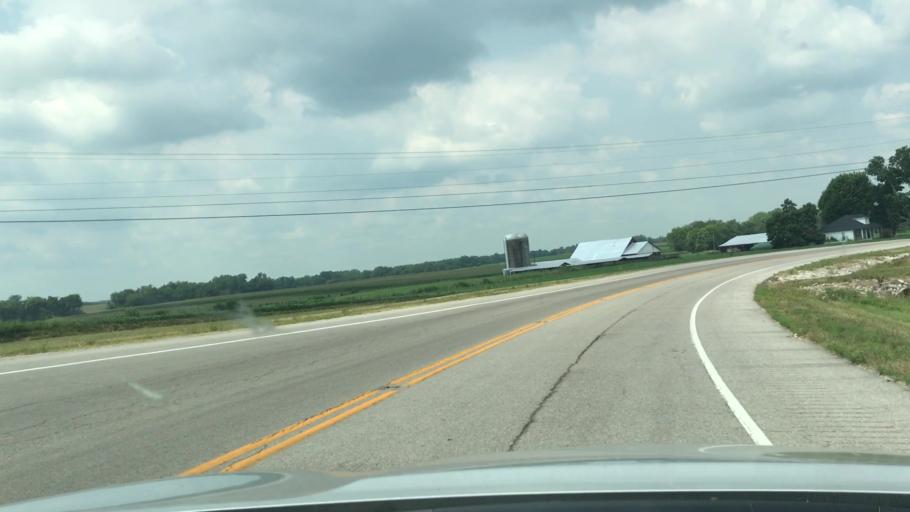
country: US
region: Kentucky
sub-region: Todd County
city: Elkton
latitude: 36.8038
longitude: -87.1214
